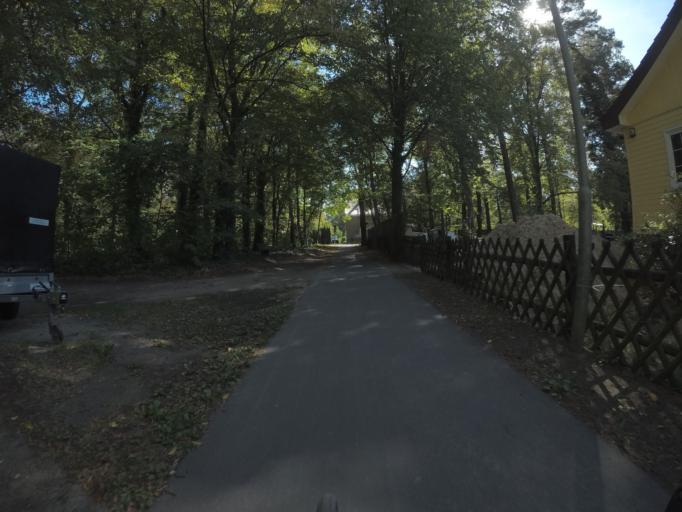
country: DE
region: Berlin
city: Falkenhagener Feld
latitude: 52.5979
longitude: 13.1456
